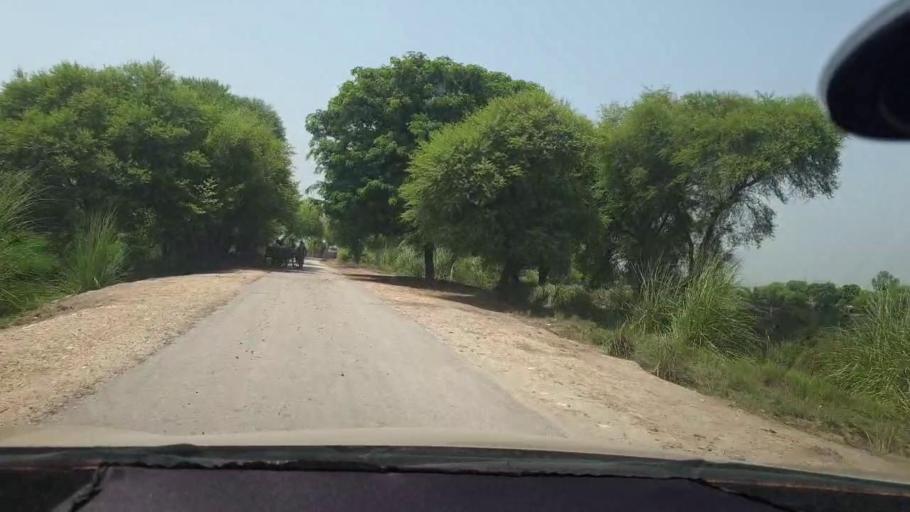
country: PK
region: Sindh
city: Kambar
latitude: 27.6623
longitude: 67.9411
